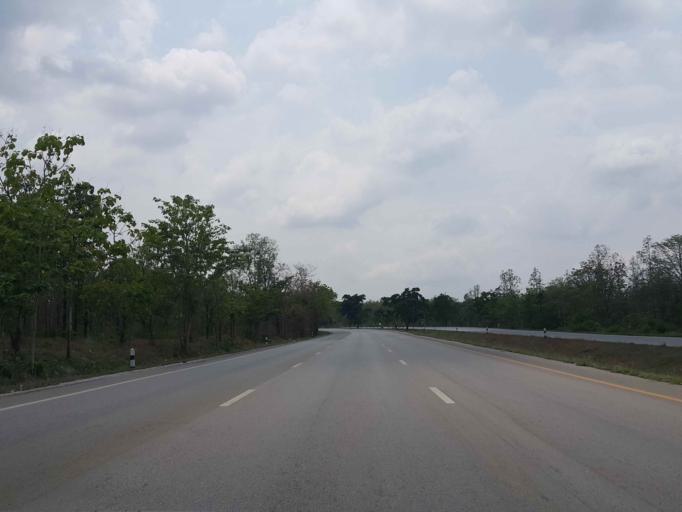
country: TH
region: Lampang
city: Ko Kha
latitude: 18.0540
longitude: 99.3882
